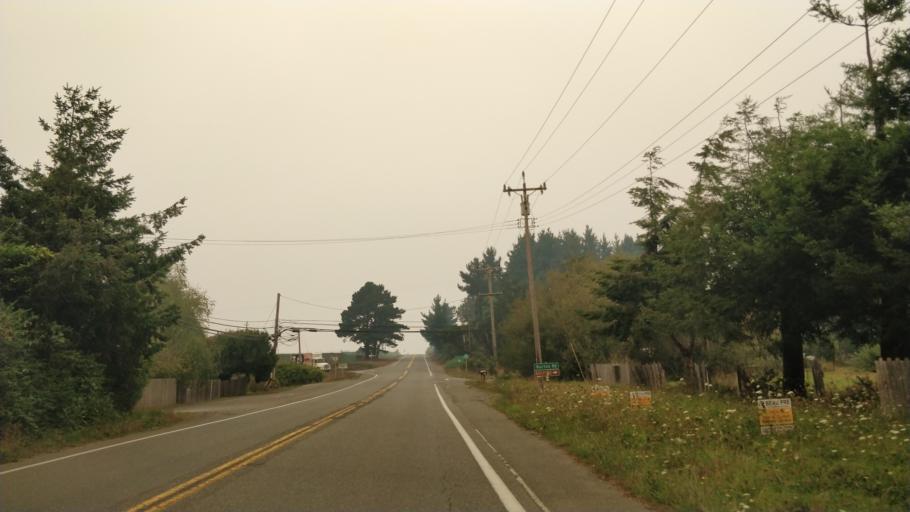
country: US
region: California
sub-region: Humboldt County
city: McKinleyville
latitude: 40.9626
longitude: -124.1009
